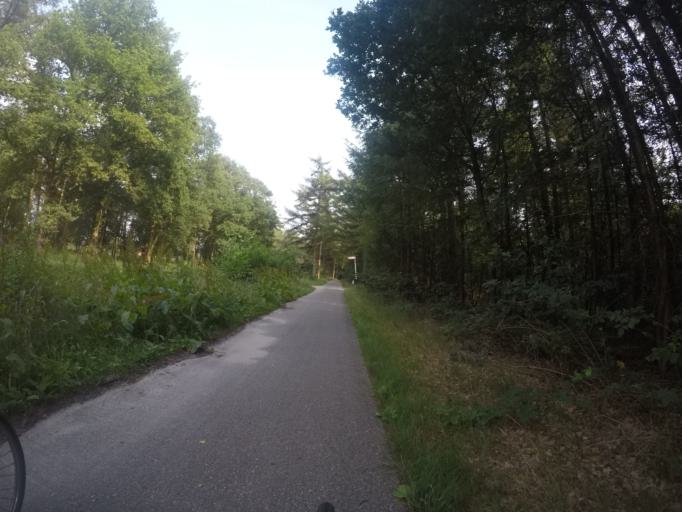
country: NL
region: Friesland
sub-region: Gemeente Weststellingwerf
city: Noordwolde
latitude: 52.8925
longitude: 6.2386
